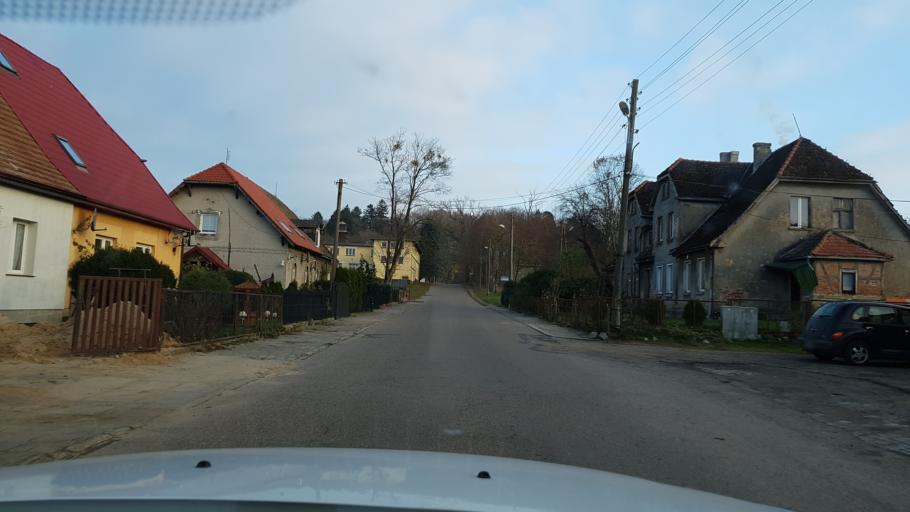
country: PL
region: West Pomeranian Voivodeship
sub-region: Koszalin
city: Koszalin
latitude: 54.1010
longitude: 16.1547
